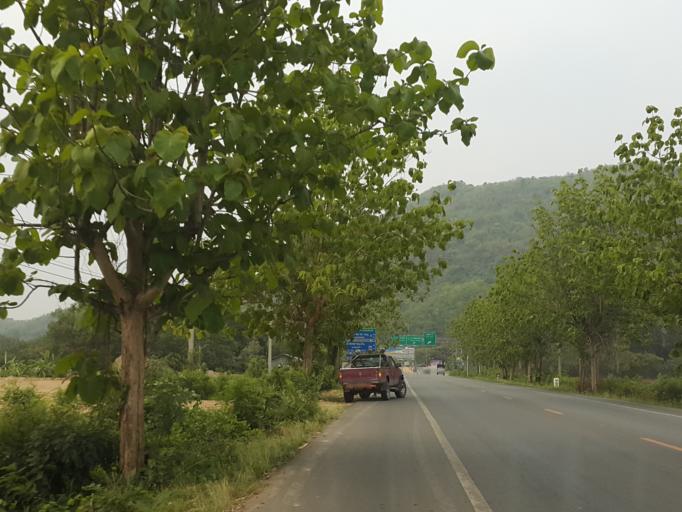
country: TH
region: Uthai Thani
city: Ban Rai
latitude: 15.0821
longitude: 99.5847
